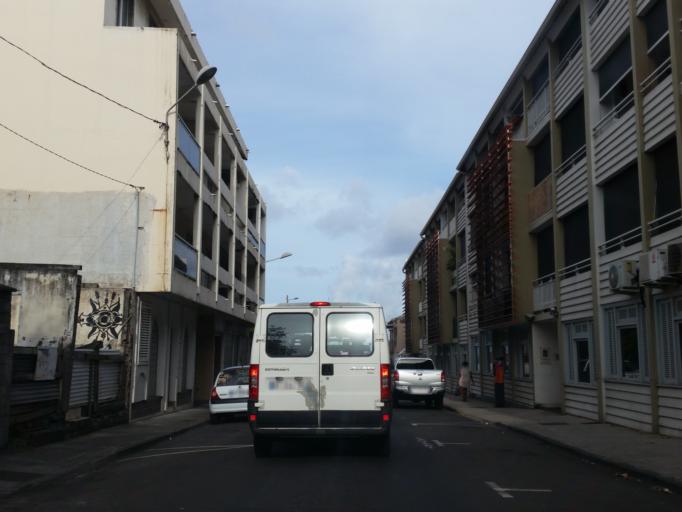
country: RE
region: Reunion
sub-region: Reunion
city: Saint-Denis
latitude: -20.8760
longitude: 55.4539
